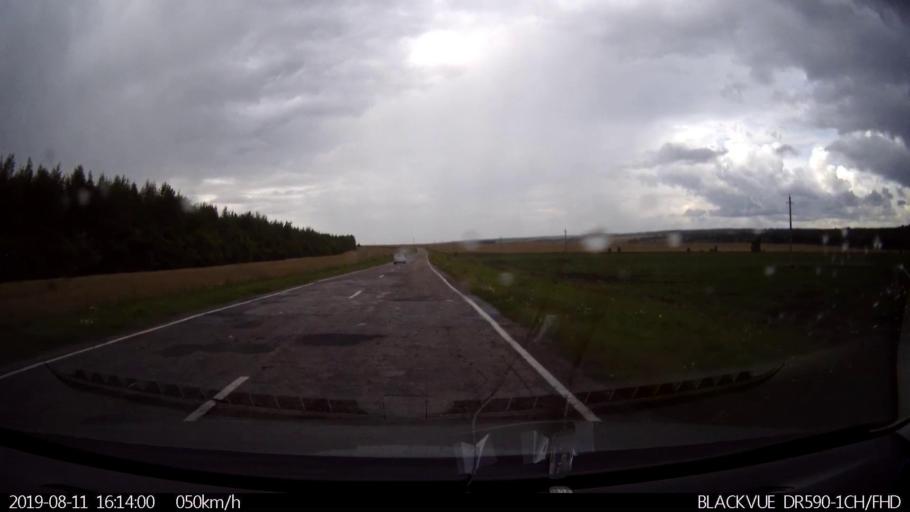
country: RU
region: Ulyanovsk
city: Ignatovka
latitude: 54.0245
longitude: 47.6352
